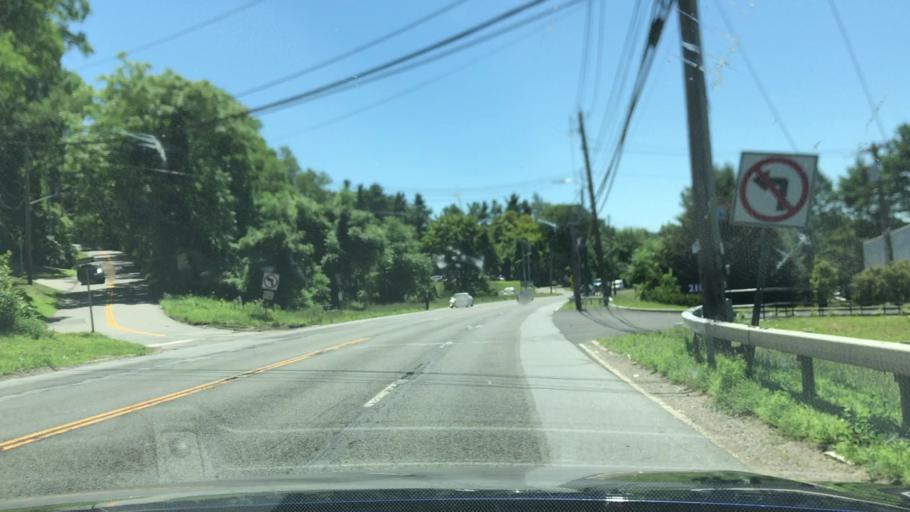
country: US
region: New York
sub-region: Westchester County
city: Hawthorne
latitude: 41.1004
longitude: -73.8079
